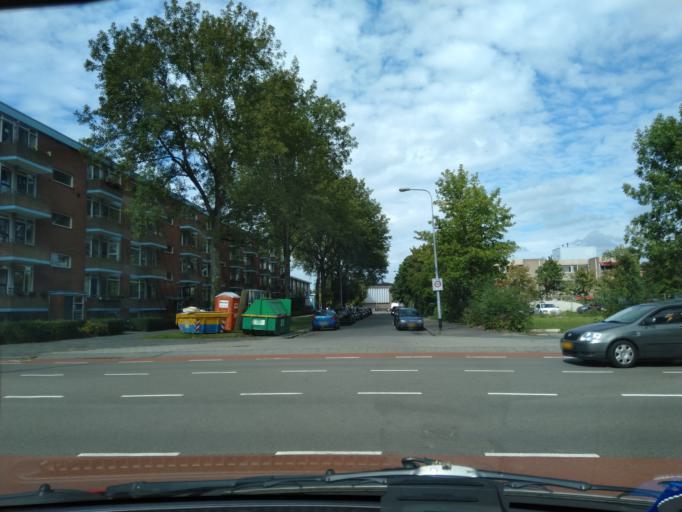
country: NL
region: Groningen
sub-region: Gemeente Groningen
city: Groningen
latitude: 53.1973
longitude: 6.5682
